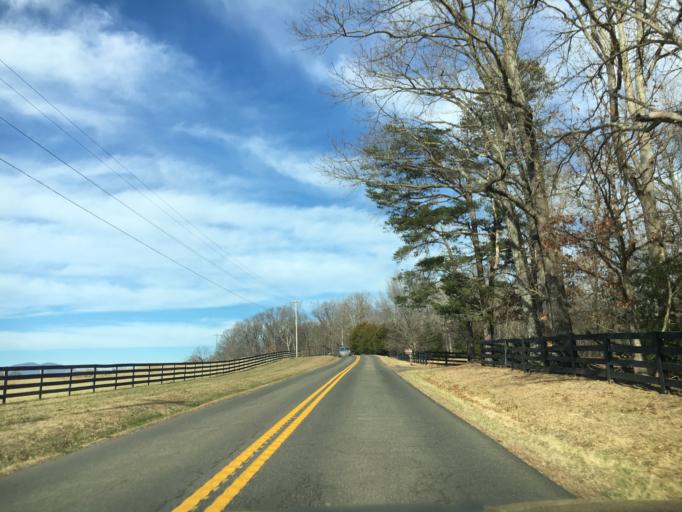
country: US
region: Virginia
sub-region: Fauquier County
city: Marshall
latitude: 38.7759
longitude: -77.9805
